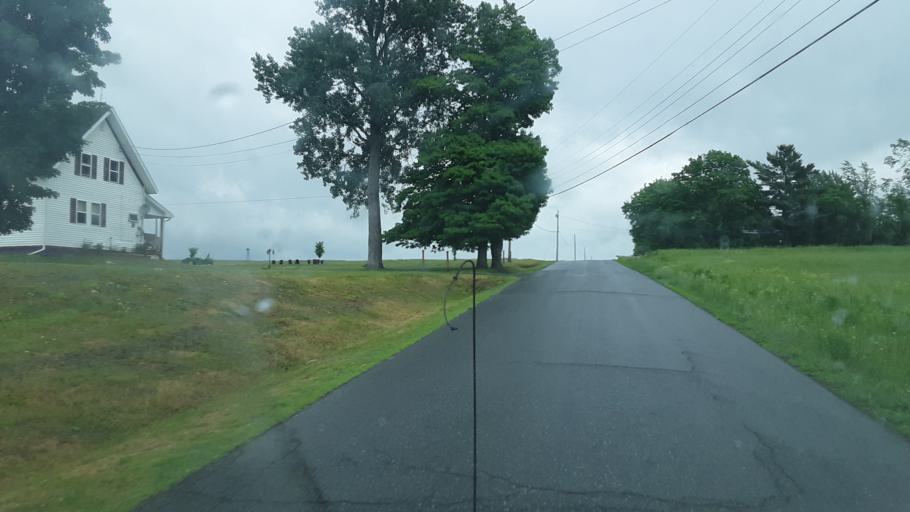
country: US
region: Maine
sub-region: Aroostook County
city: Presque Isle
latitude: 46.6817
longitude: -68.1897
